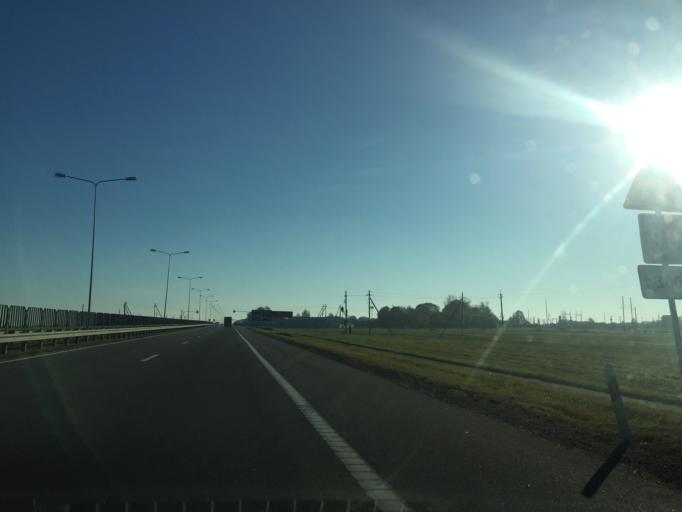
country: BY
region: Minsk
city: Smilavichy
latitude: 53.7595
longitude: 27.9988
